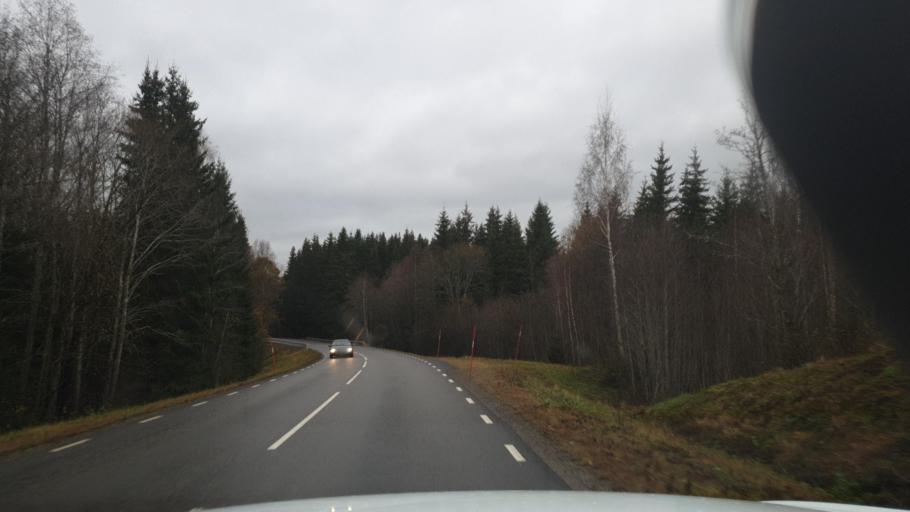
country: SE
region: Vaermland
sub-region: Eda Kommun
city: Amotfors
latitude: 59.8707
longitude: 12.5431
